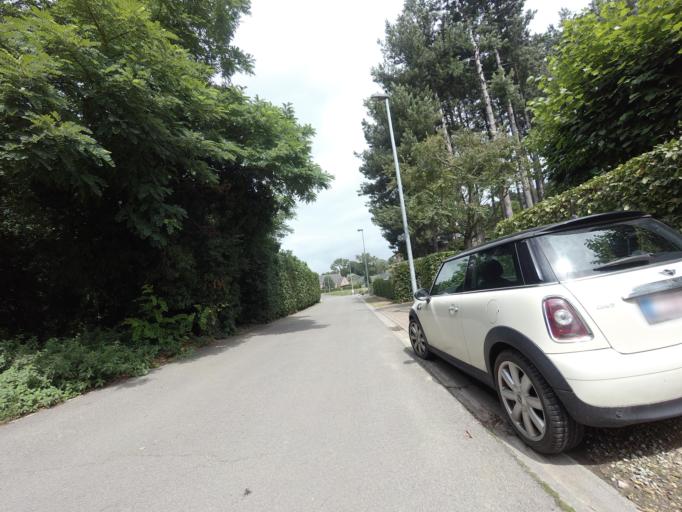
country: BE
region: Flanders
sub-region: Provincie Antwerpen
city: Mechelen
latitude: 51.0483
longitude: 4.4968
